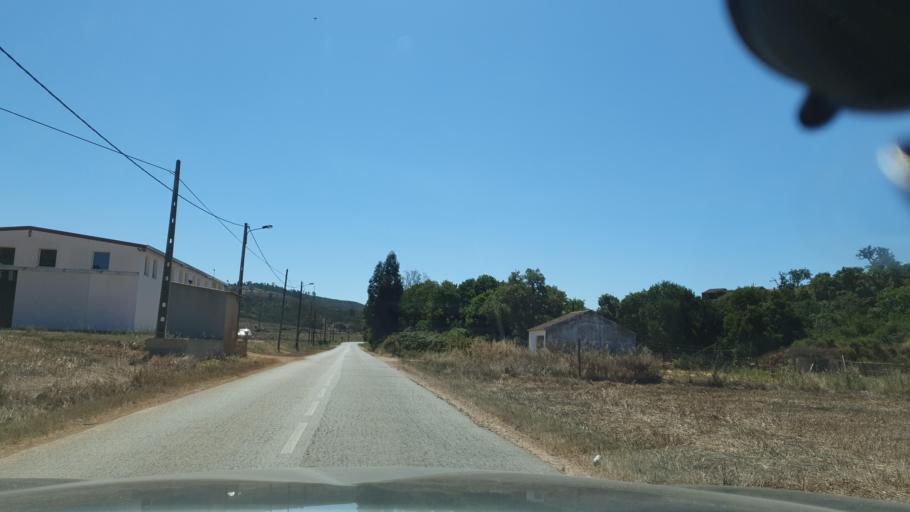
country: PT
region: Beja
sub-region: Odemira
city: Sao Teotonio
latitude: 37.4874
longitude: -8.6381
